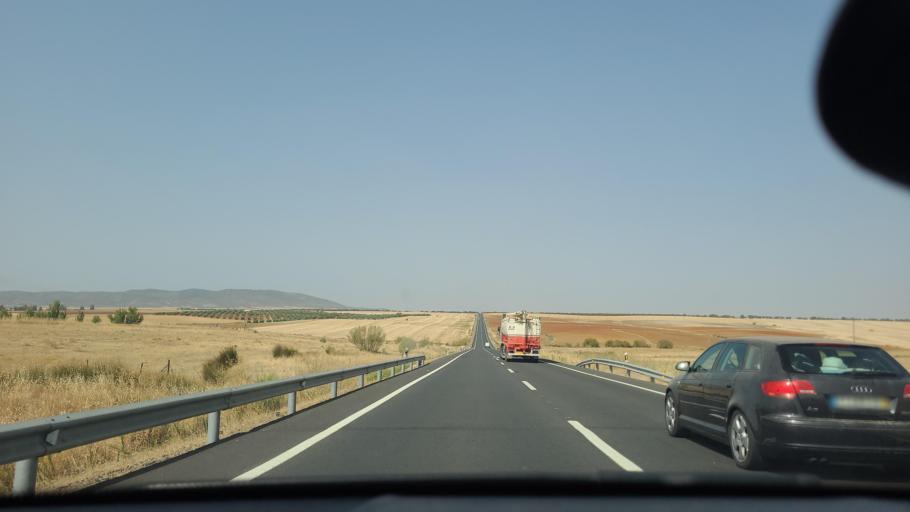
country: ES
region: Extremadura
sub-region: Provincia de Badajoz
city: Ahillones
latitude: 38.2548
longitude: -5.9078
